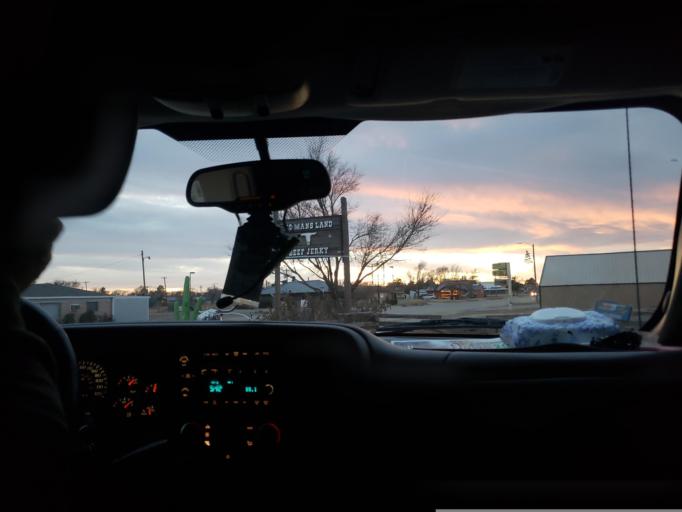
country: US
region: Oklahoma
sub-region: Cimarron County
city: Boise City
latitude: 36.7300
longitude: -102.5012
